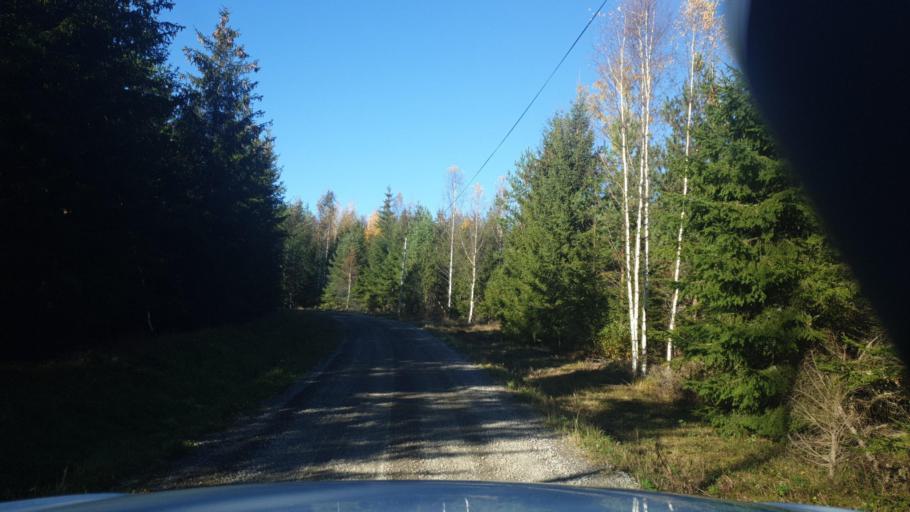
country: SE
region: Vaermland
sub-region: Arvika Kommun
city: Arvika
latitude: 59.5585
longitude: 12.8460
